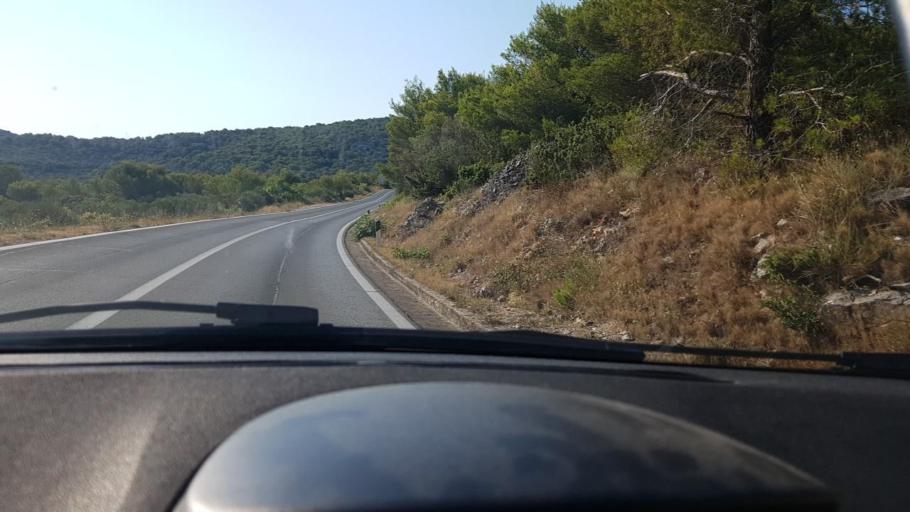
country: HR
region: Sibensko-Kniniska
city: Murter
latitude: 43.8066
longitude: 15.6075
